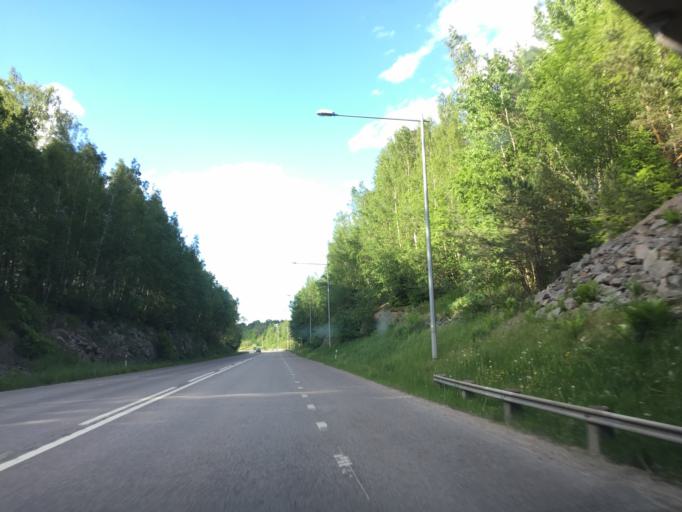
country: SE
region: OErebro
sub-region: Orebro Kommun
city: Orebro
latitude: 59.2474
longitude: 15.2371
